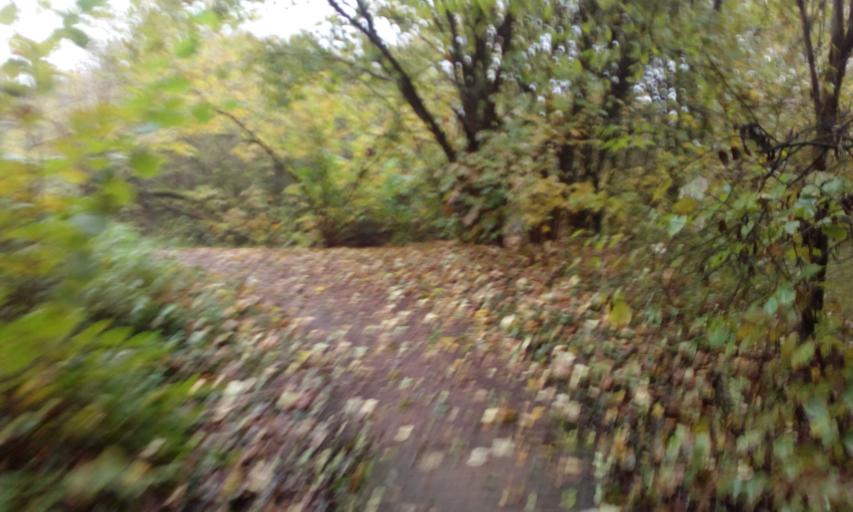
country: NL
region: South Holland
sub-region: Gemeente Lansingerland
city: Bergschenhoek
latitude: 51.9688
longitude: 4.5052
